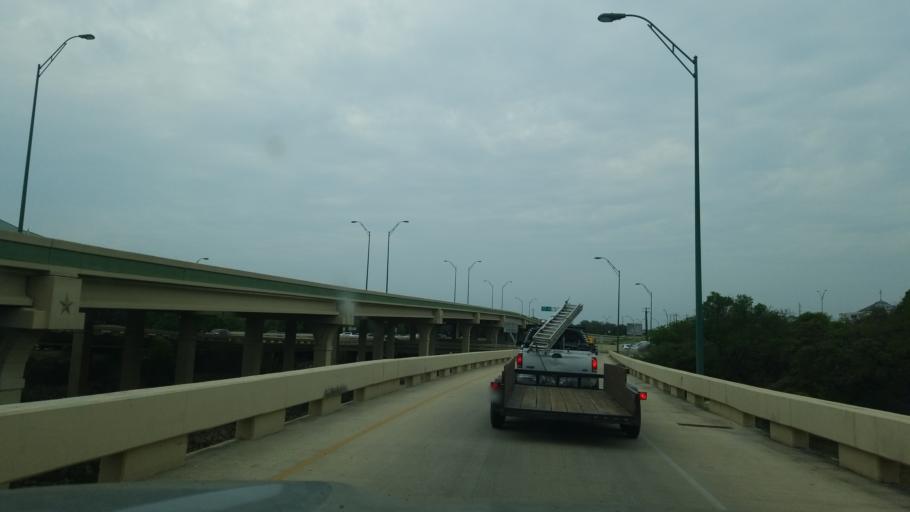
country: US
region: Texas
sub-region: Bexar County
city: Castle Hills
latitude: 29.5542
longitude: -98.4839
